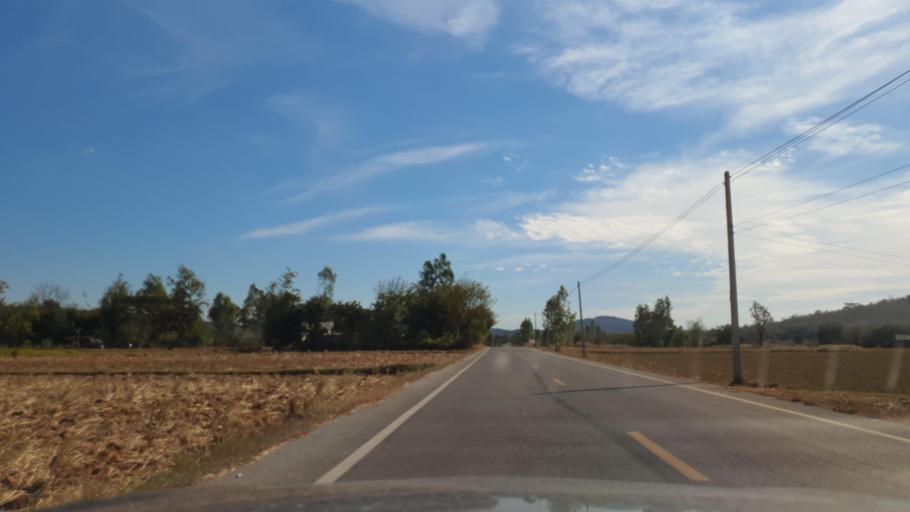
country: TH
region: Kalasin
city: Khao Wong
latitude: 16.6100
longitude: 104.1355
